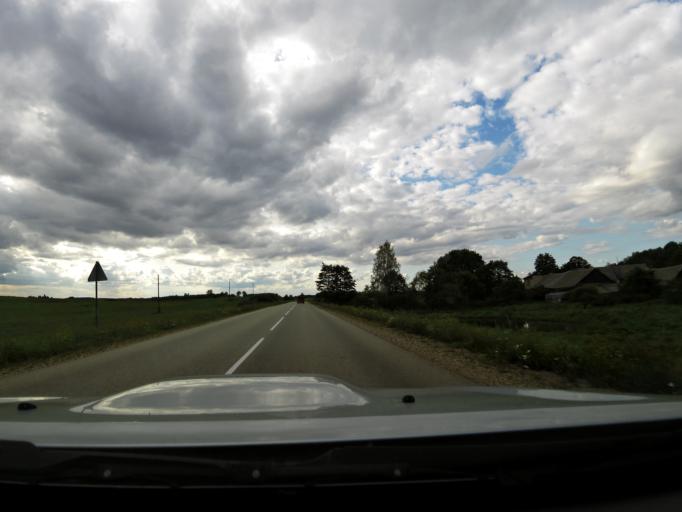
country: LV
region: Ilukste
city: Ilukste
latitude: 55.9810
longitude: 26.0018
